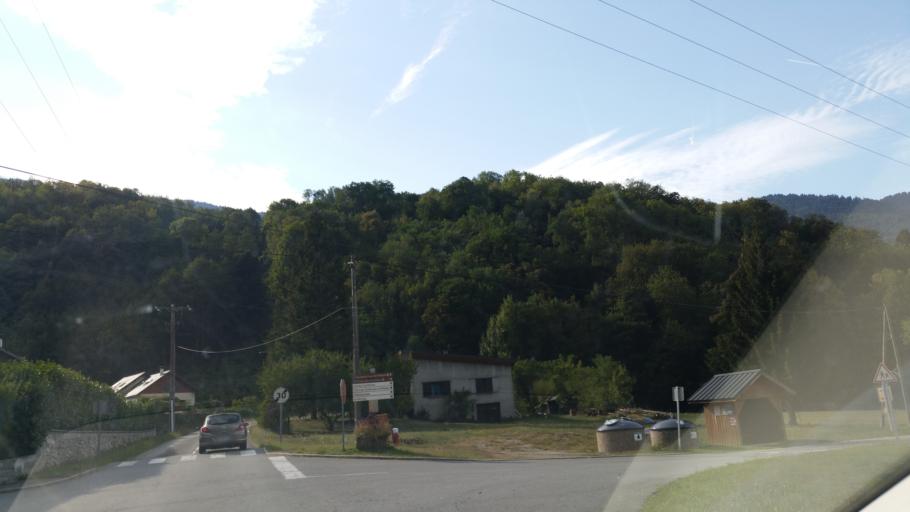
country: FR
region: Rhone-Alpes
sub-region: Departement de la Savoie
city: Saint-Remy-de-Maurienne
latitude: 45.4735
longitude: 6.2807
